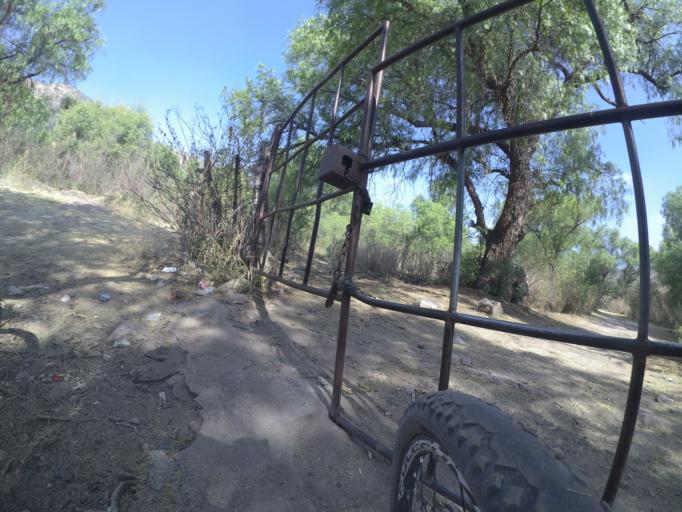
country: MX
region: Aguascalientes
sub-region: Jesus Maria
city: Paseos de las Haciendas [Fraccionamiento]
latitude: 22.0034
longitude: -102.3683
